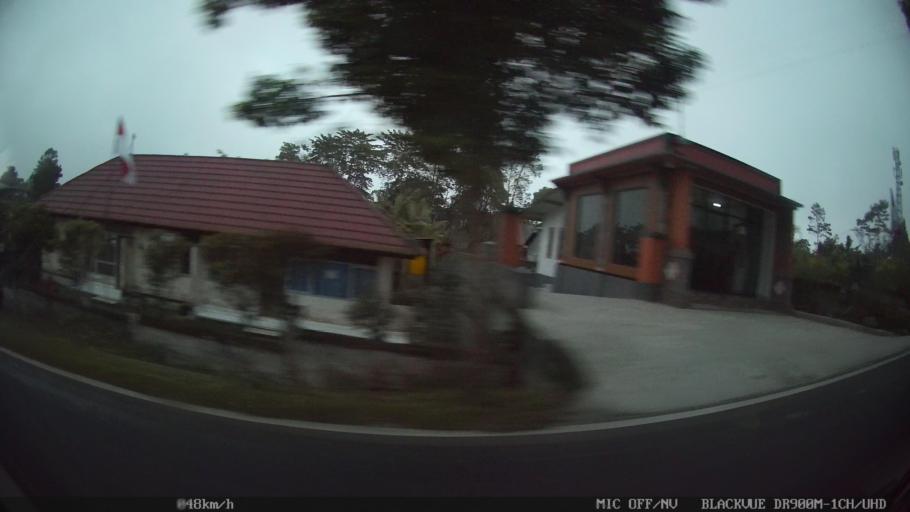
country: ID
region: Bali
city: Banjar Taro Kelod
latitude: -8.3131
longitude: 115.3019
